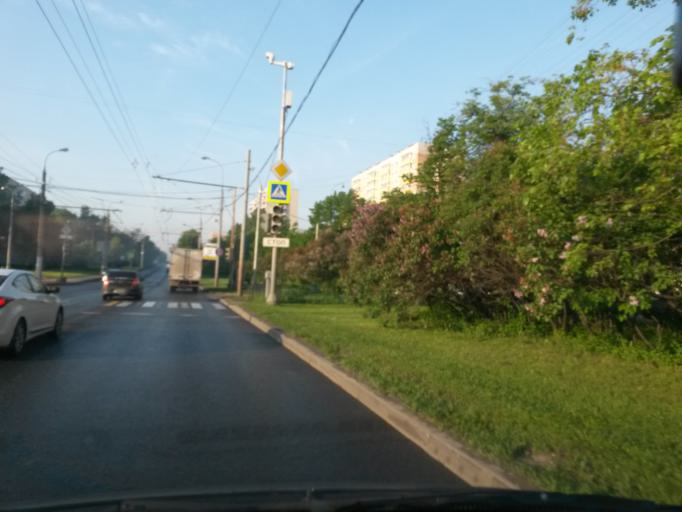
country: RU
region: Moscow
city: Metrogorodok
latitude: 55.8202
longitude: 37.7979
